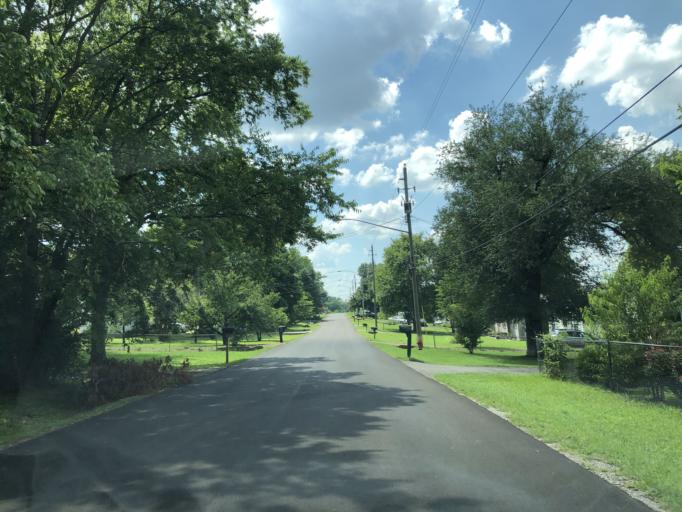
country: US
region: Tennessee
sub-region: Davidson County
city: Oak Hill
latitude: 36.1196
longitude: -86.7348
